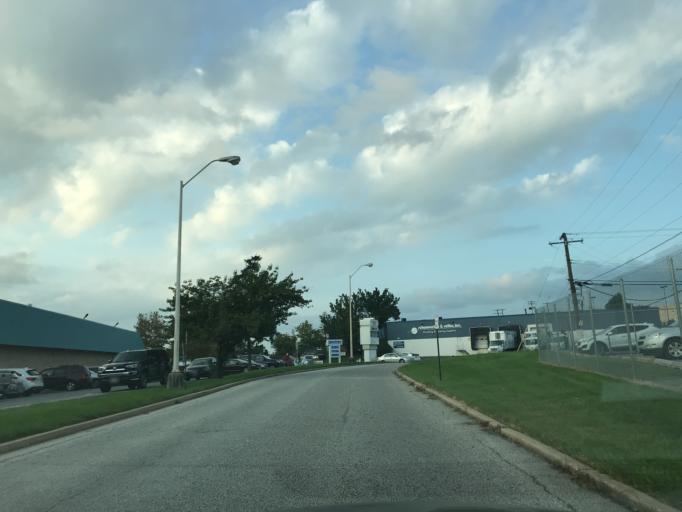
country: US
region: Maryland
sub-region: Baltimore County
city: Timonium
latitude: 39.4325
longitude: -76.6261
